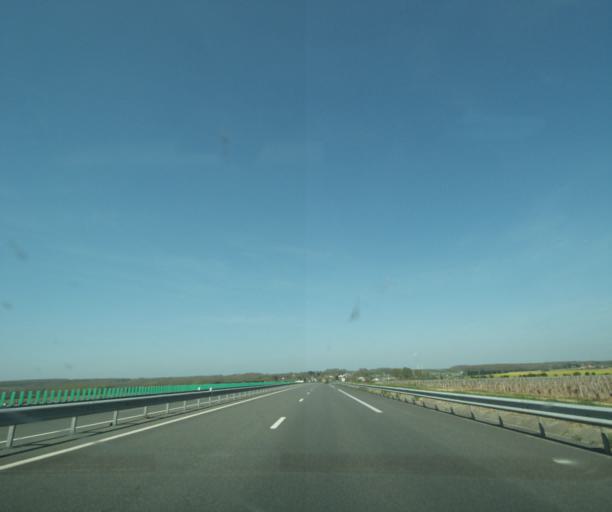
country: FR
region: Bourgogne
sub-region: Departement de la Nievre
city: Pouilly-sur-Loire
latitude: 47.3251
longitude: 2.9327
